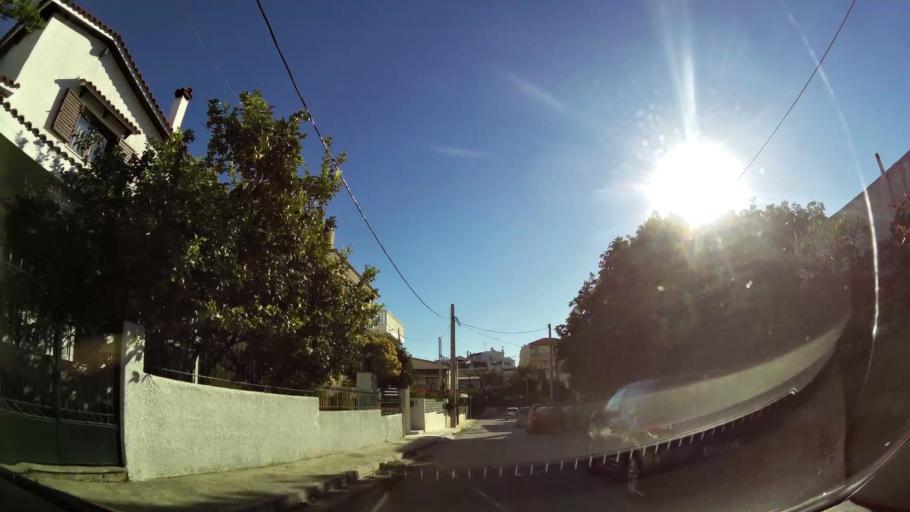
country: GR
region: Attica
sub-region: Nomarchia Anatolikis Attikis
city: Gerakas
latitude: 38.0104
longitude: 23.8529
